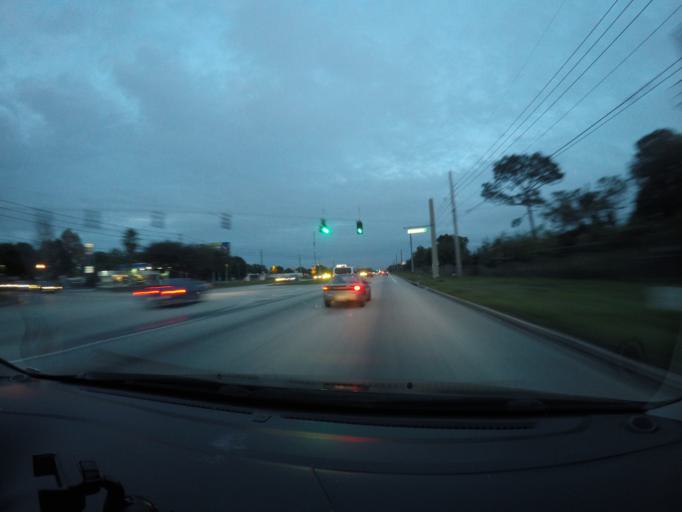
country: US
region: Florida
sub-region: Orange County
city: Tangelo Park
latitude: 28.4499
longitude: -81.4464
